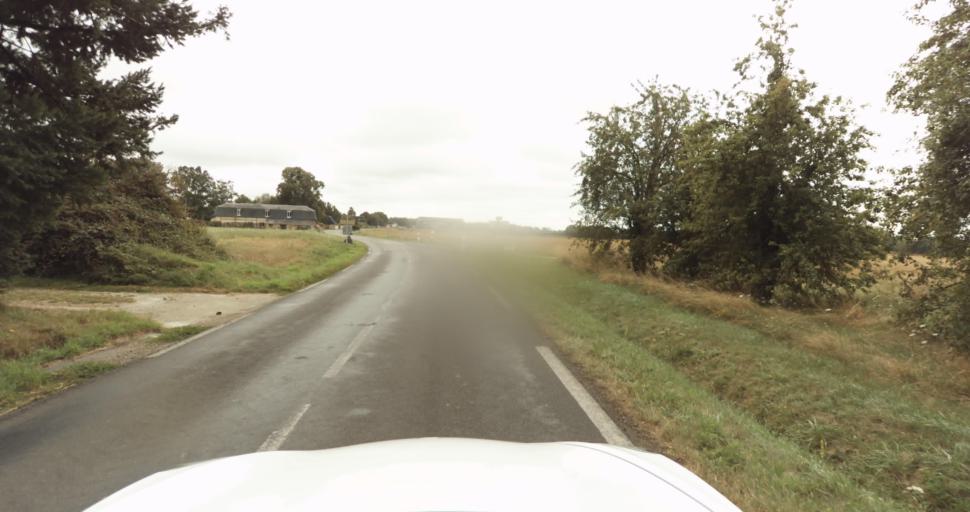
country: FR
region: Haute-Normandie
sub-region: Departement de l'Eure
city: Aviron
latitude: 49.0675
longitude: 1.0687
